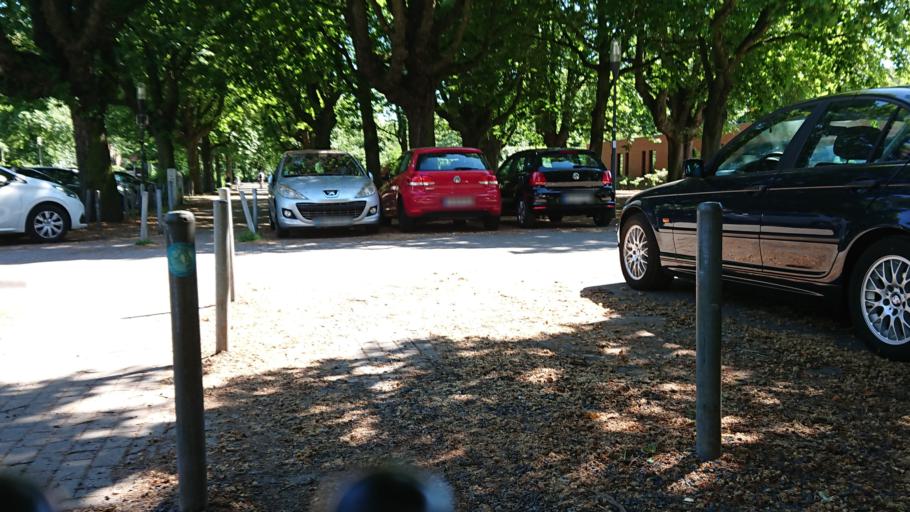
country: DE
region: North Rhine-Westphalia
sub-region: Regierungsbezirk Koln
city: Neuehrenfeld
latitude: 50.9354
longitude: 6.9172
